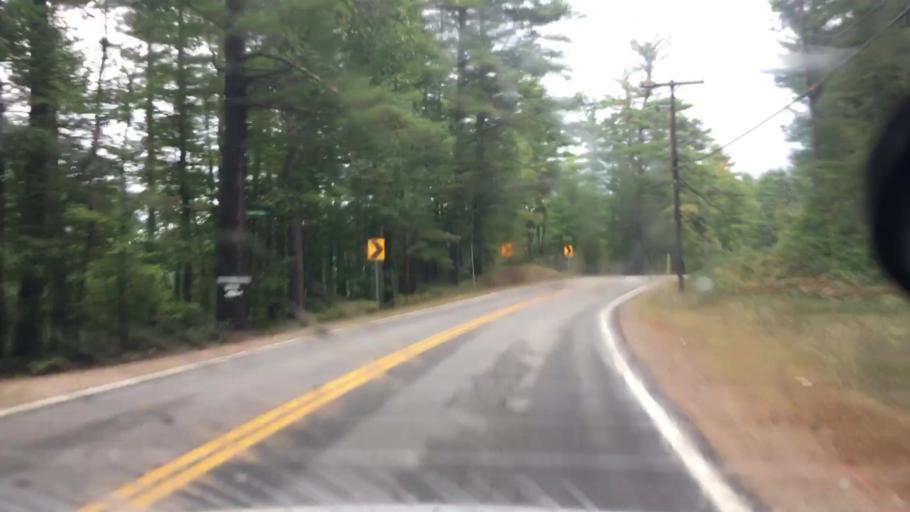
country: US
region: New Hampshire
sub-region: Carroll County
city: Wakefield
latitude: 43.6275
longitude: -70.9870
